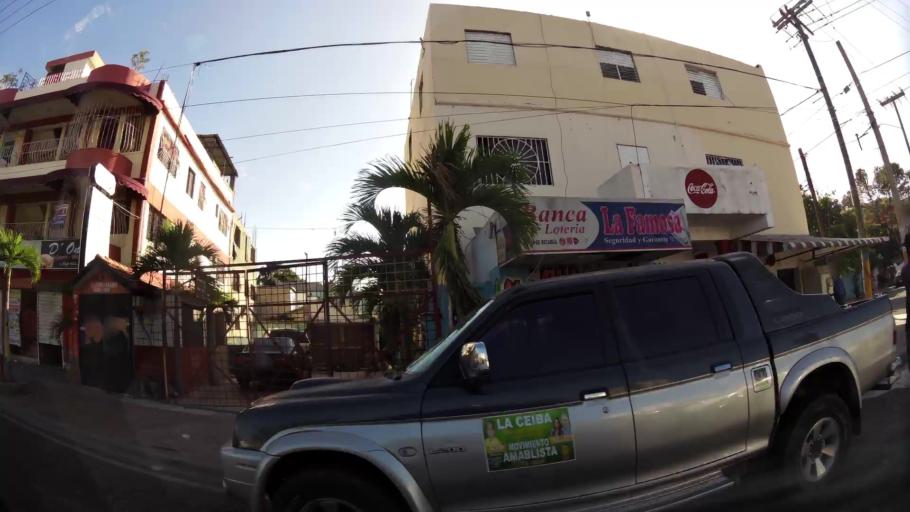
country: DO
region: Nacional
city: San Carlos
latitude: 18.4759
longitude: -69.8778
